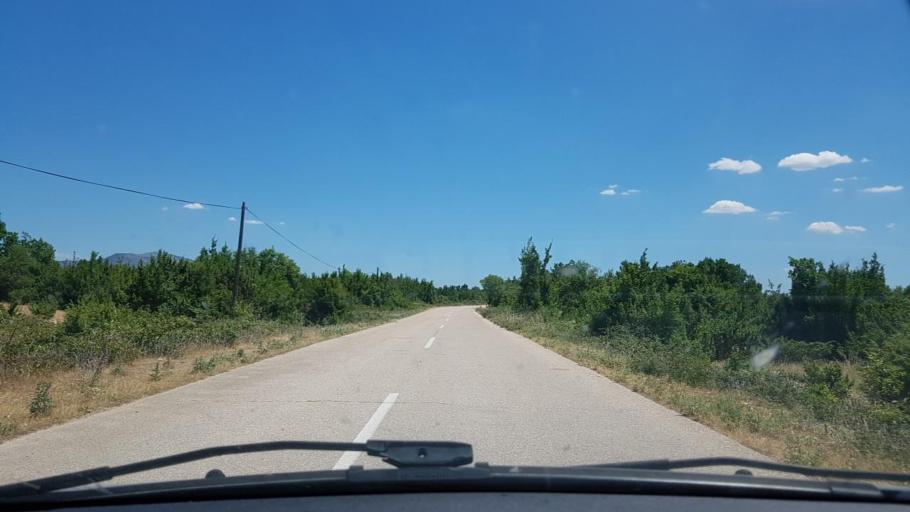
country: HR
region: Sibensko-Kniniska
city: Kistanje
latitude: 43.9686
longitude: 15.9773
